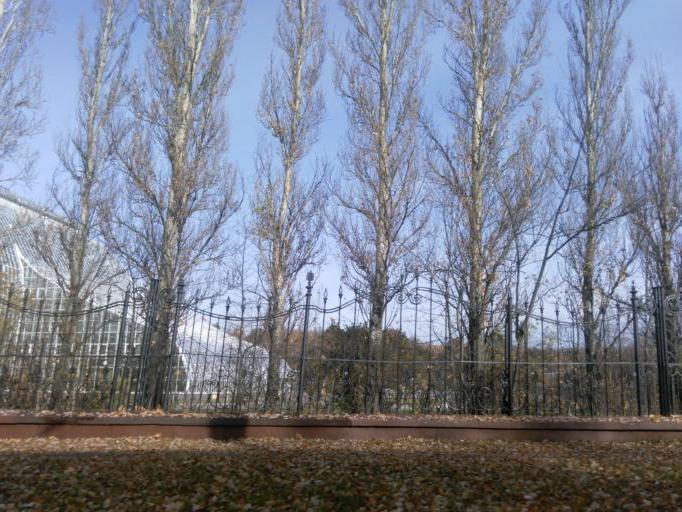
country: RU
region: Moscow
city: Novovladykino
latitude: 55.8341
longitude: 37.5944
